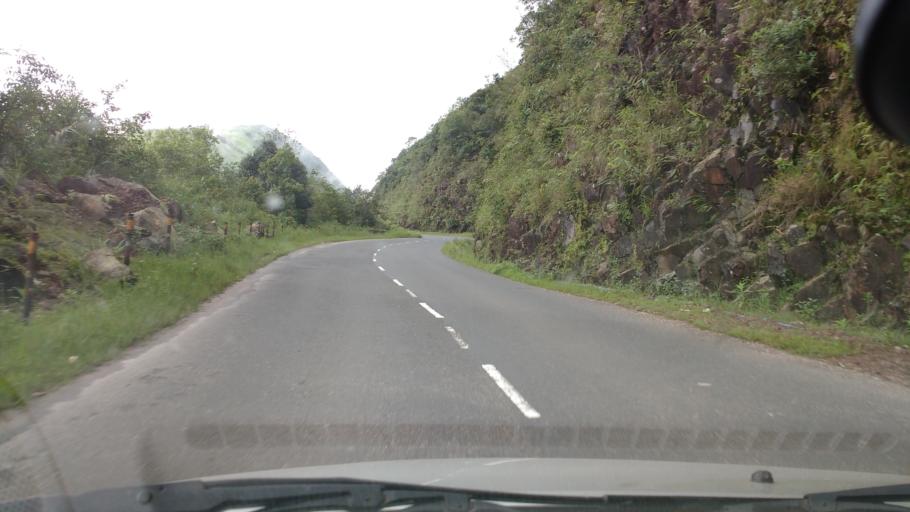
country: IN
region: Meghalaya
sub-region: East Khasi Hills
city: Shillong
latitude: 25.3804
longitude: 91.8735
